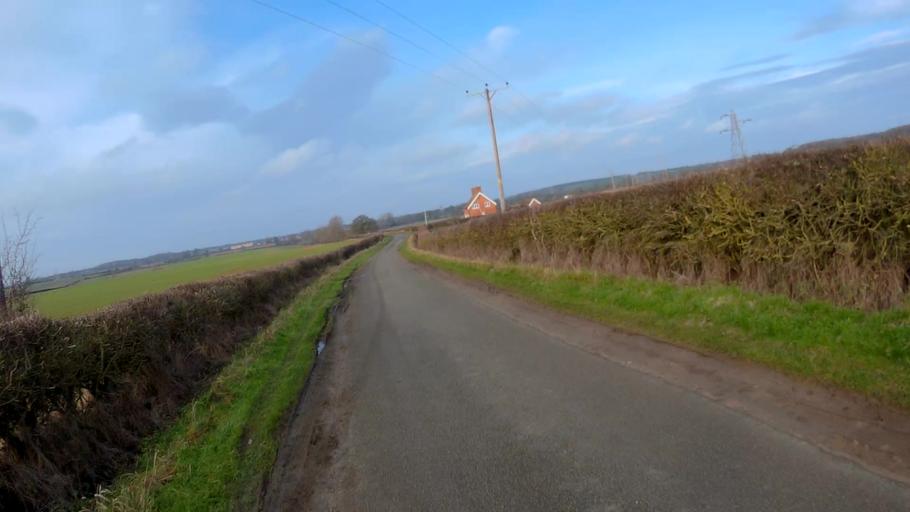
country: GB
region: England
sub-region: Lincolnshire
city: Bourne
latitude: 52.7670
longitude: -0.4218
